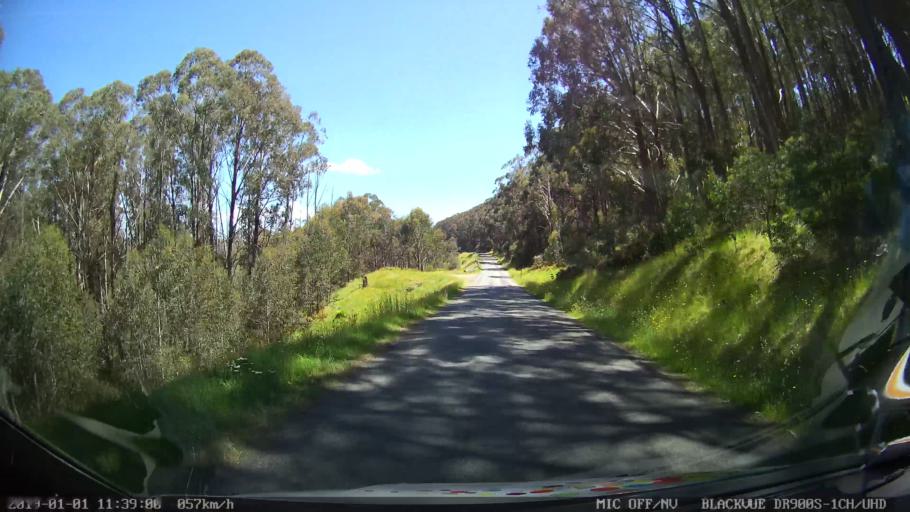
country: AU
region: New South Wales
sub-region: Snowy River
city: Jindabyne
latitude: -35.9301
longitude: 148.3864
